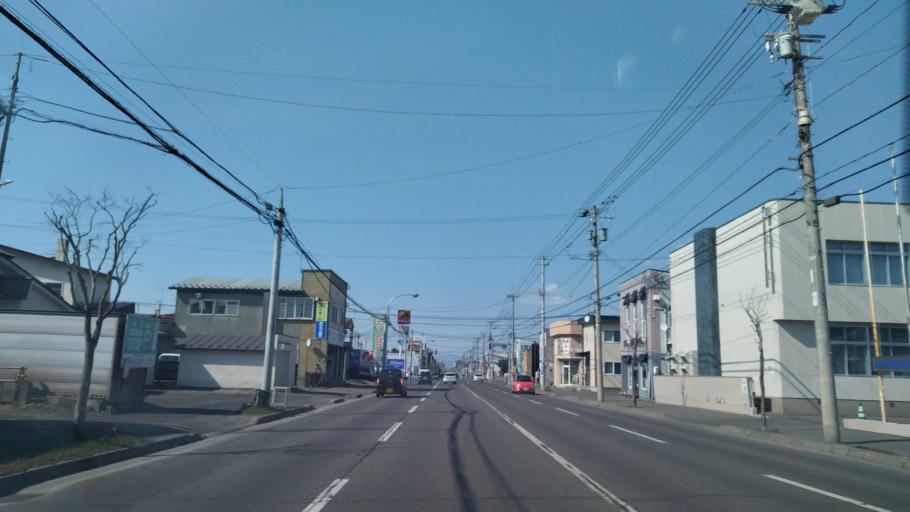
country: JP
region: Hokkaido
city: Obihiro
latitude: 42.8978
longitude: 143.2006
